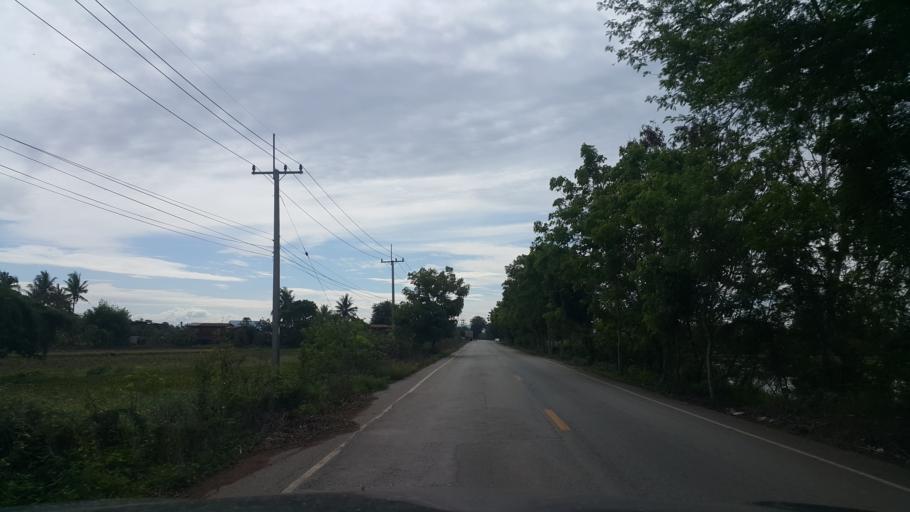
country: TH
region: Sukhothai
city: Si Nakhon
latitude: 17.2793
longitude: 99.9981
